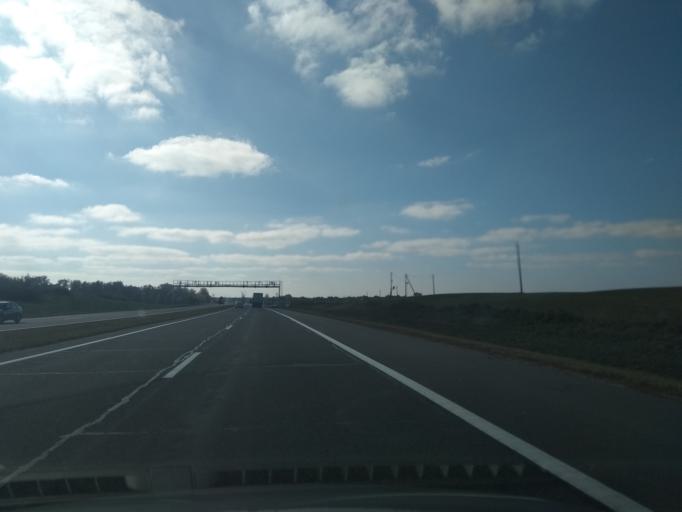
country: BY
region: Brest
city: Baranovichi
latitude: 53.1323
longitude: 25.9160
